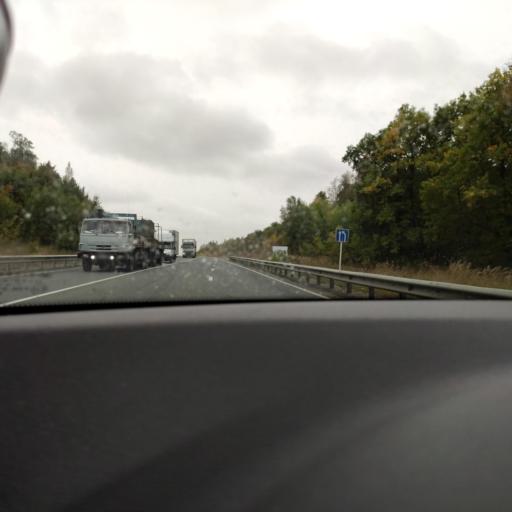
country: RU
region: Samara
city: Mirnyy
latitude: 53.6017
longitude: 50.2756
